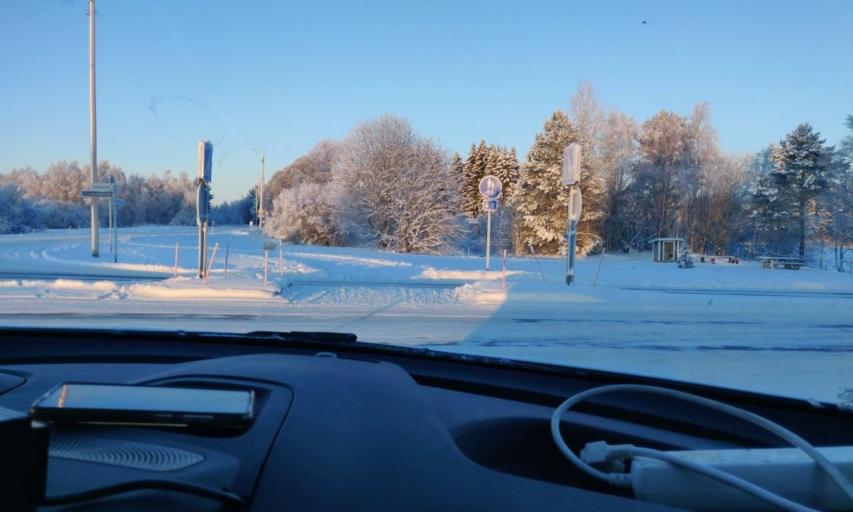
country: FI
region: Northern Ostrobothnia
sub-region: Raahe
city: Siikajoki
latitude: 64.8156
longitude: 24.7673
